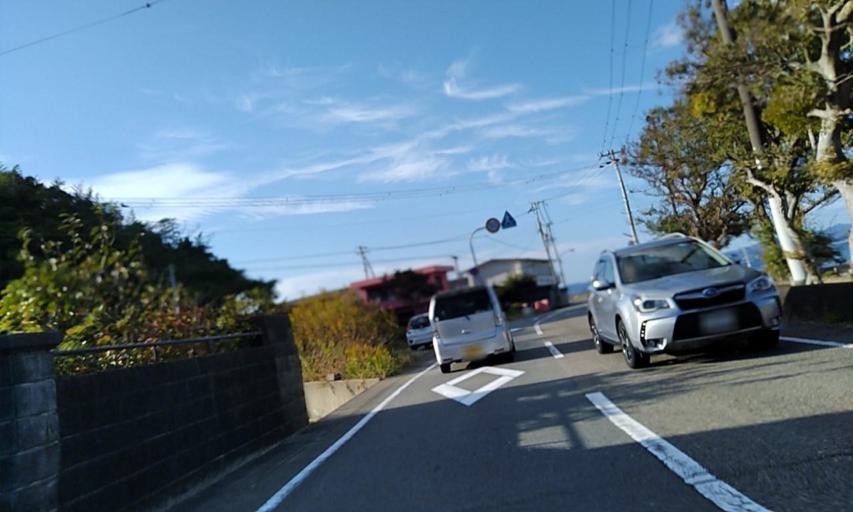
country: JP
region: Wakayama
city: Tanabe
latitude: 33.6932
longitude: 135.3499
